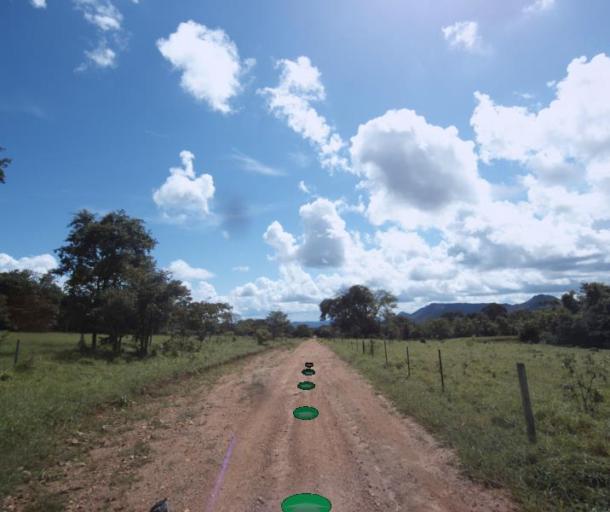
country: BR
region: Goias
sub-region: Pirenopolis
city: Pirenopolis
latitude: -15.7843
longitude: -48.9293
